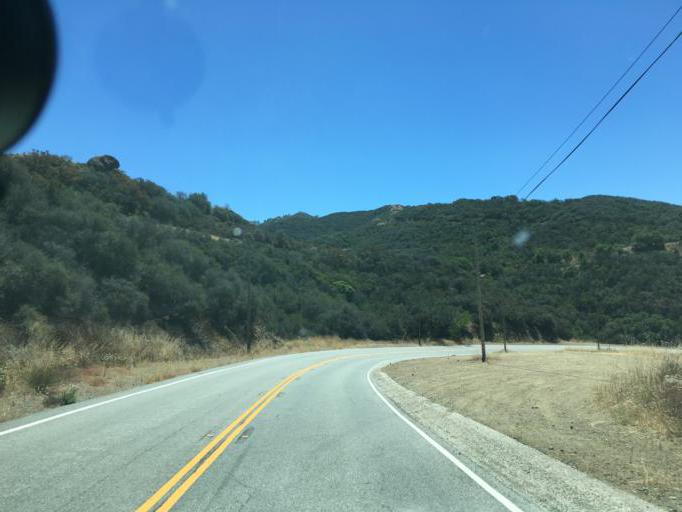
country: US
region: California
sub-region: Los Angeles County
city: Westlake Village
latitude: 34.0891
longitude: -118.8390
